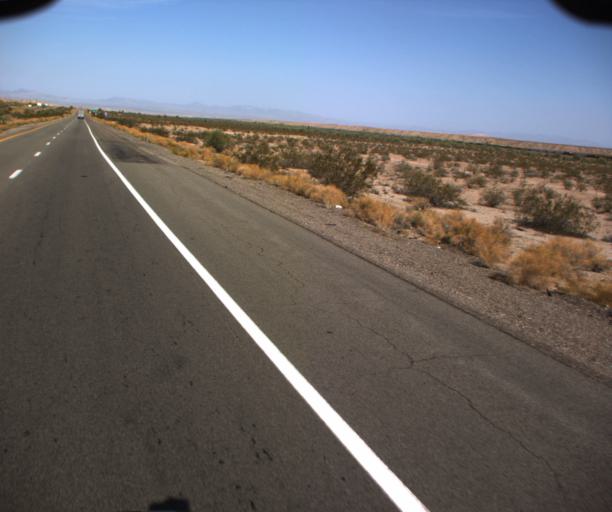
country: US
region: Arizona
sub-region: Mohave County
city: Desert Hills
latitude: 34.7296
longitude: -114.3239
